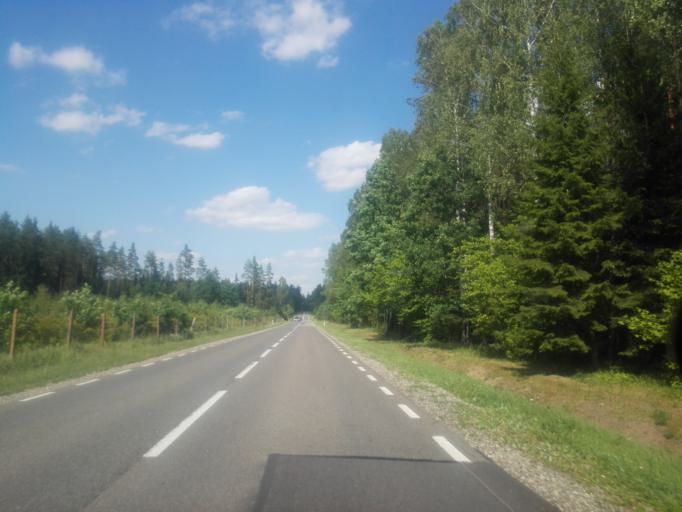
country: PL
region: Podlasie
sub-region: Powiat sejnenski
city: Sejny
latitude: 54.0032
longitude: 23.3184
